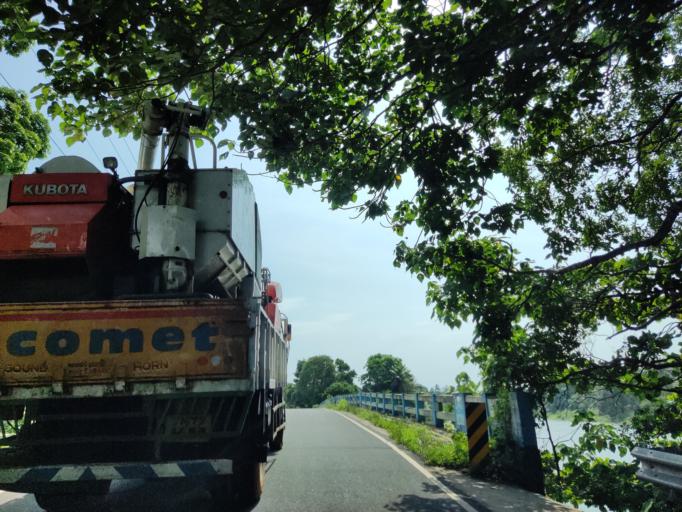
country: IN
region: Kerala
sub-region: Alappuzha
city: Mavelikara
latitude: 9.3249
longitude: 76.4652
